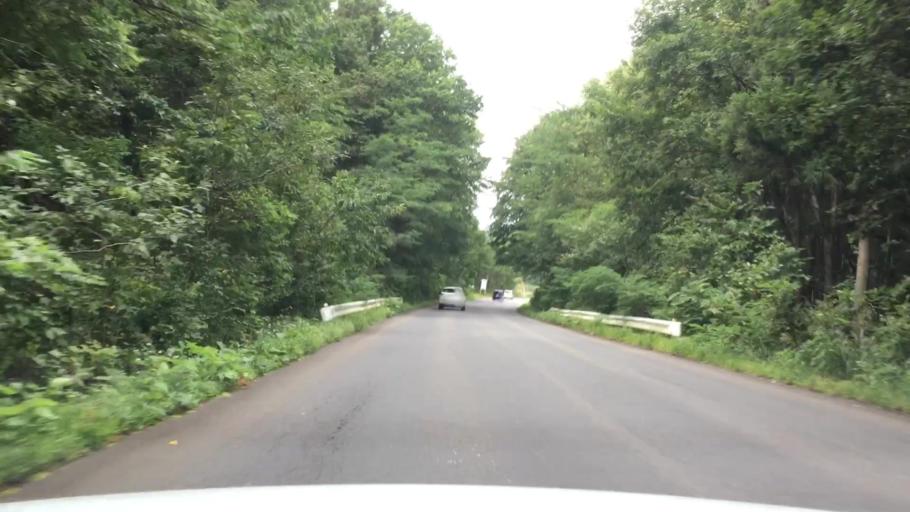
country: JP
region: Aomori
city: Shimokizukuri
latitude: 40.7123
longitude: 140.2670
